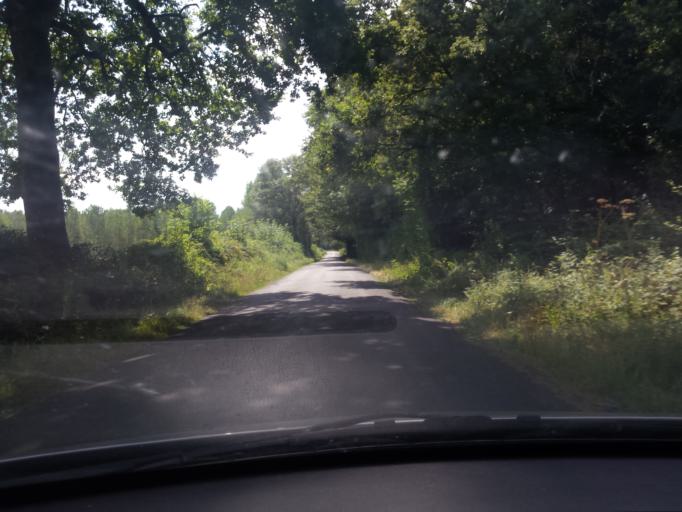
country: FR
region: Poitou-Charentes
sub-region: Departement de la Vienne
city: Availles-Limouzine
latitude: 46.1154
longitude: 0.6735
